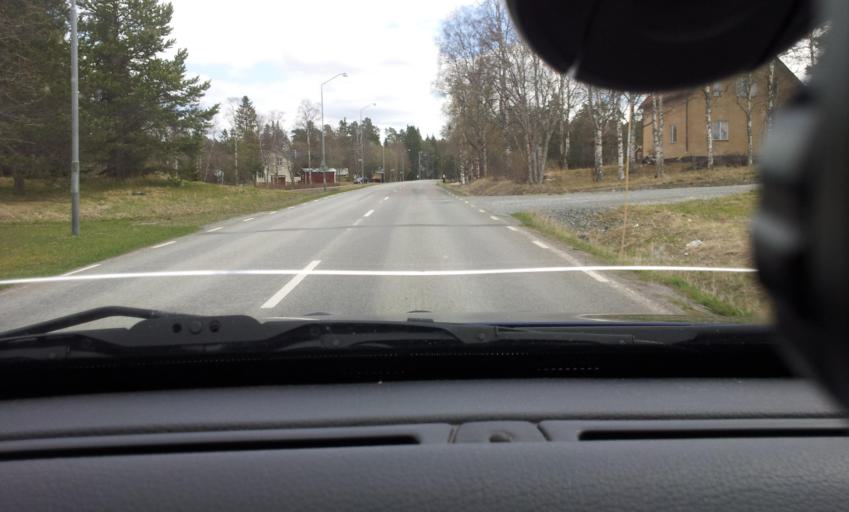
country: SE
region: Jaemtland
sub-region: OEstersunds Kommun
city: Ostersund
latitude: 63.1498
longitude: 14.6002
